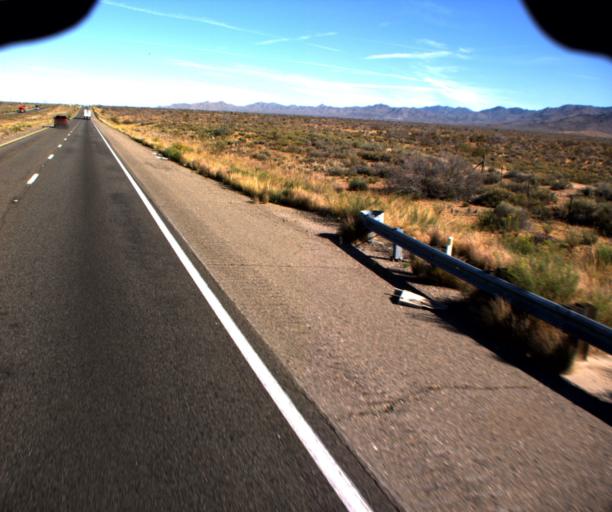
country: US
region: Arizona
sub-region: Mohave County
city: Golden Valley
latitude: 35.3035
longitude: -114.1915
